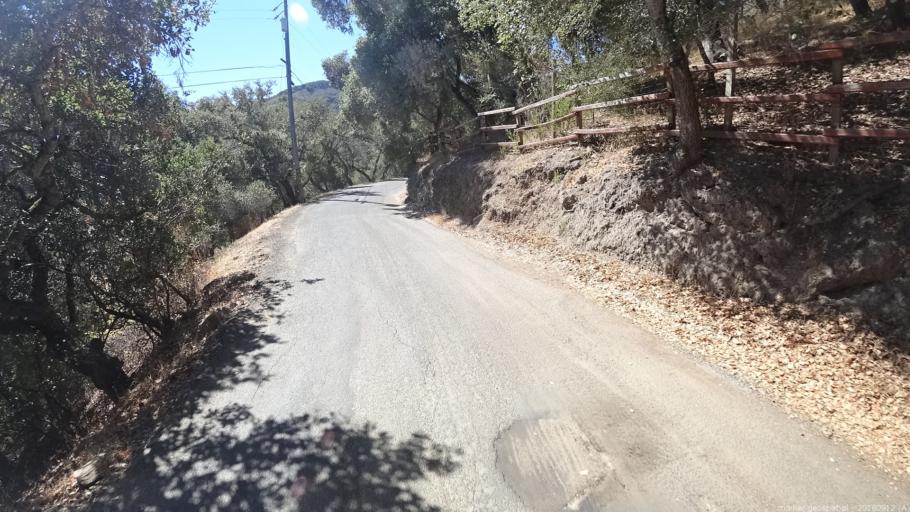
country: US
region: California
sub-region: Monterey County
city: Carmel Valley Village
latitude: 36.4635
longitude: -121.7285
